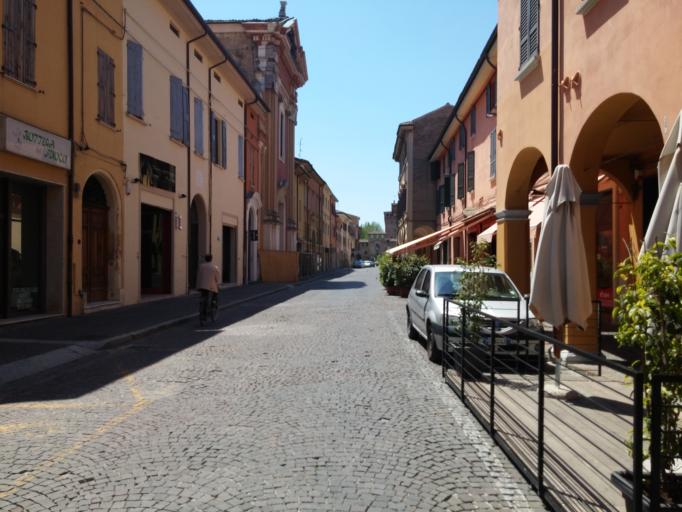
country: IT
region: Emilia-Romagna
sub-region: Provincia di Ferrara
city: Cento
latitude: 44.7266
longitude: 11.2892
